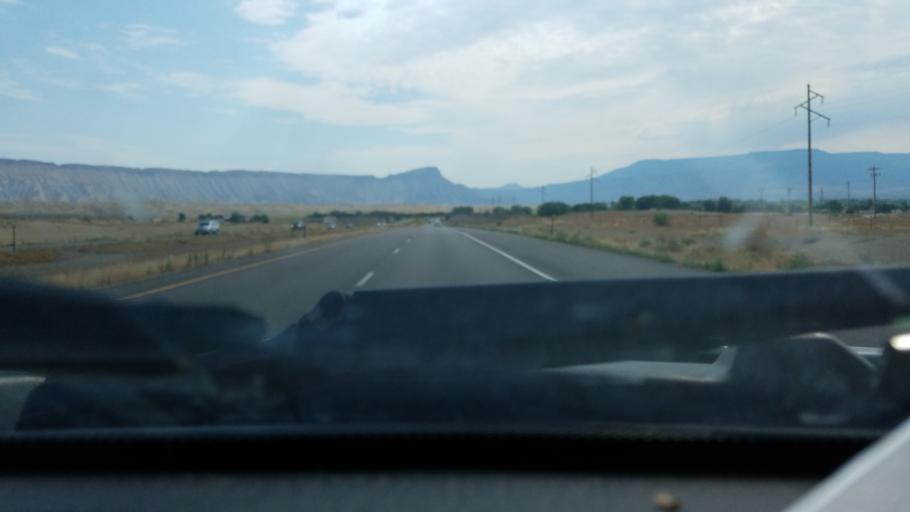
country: US
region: Colorado
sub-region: Mesa County
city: Fruitvale
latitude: 39.1068
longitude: -108.5183
